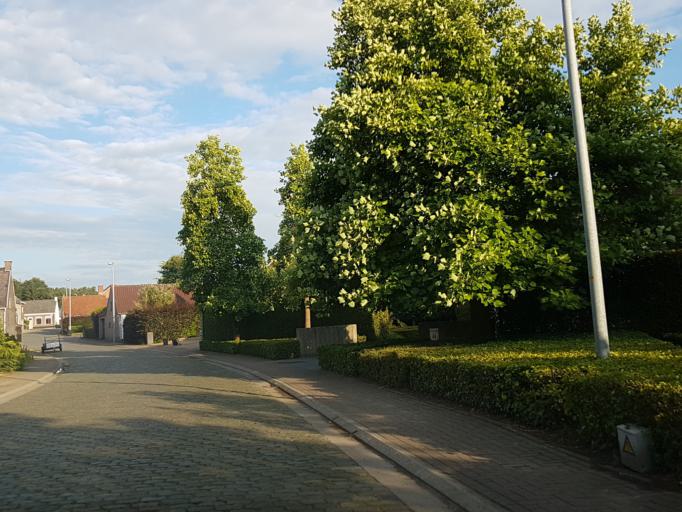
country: BE
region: Flanders
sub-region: Provincie Oost-Vlaanderen
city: Lebbeke
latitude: 50.9445
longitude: 4.1157
